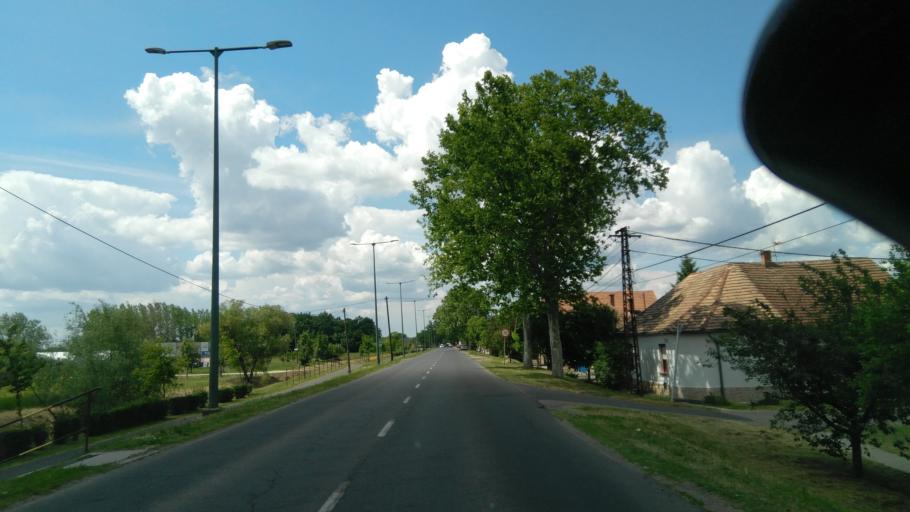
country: HU
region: Bekes
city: Gyula
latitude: 46.6487
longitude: 21.2502
